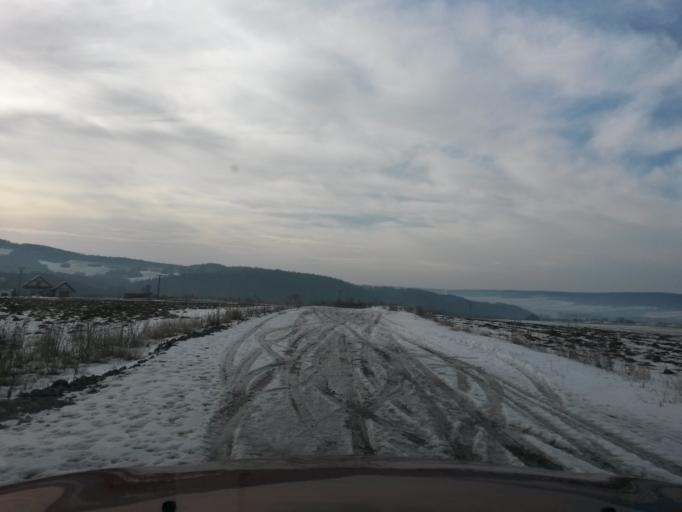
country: SK
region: Kosicky
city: Kosice
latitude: 48.7938
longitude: 21.3444
